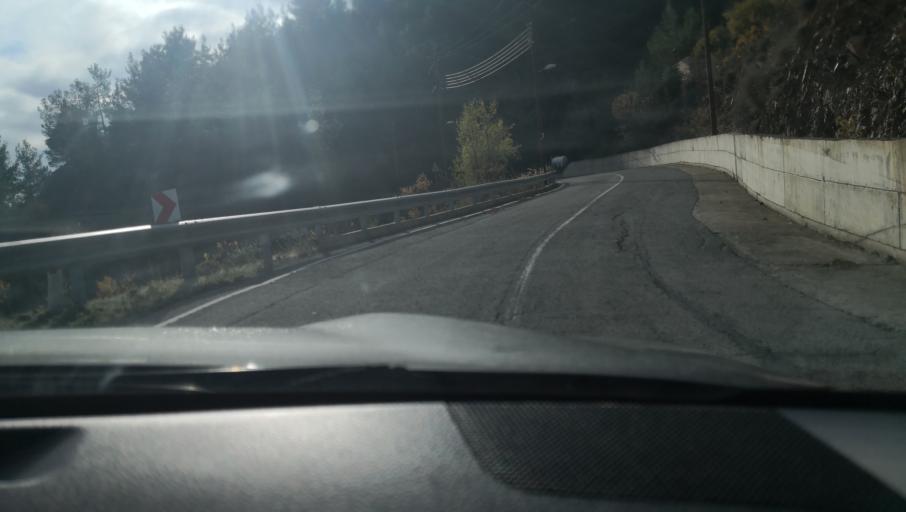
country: CY
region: Lefkosia
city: Lefka
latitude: 35.0223
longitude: 32.7242
